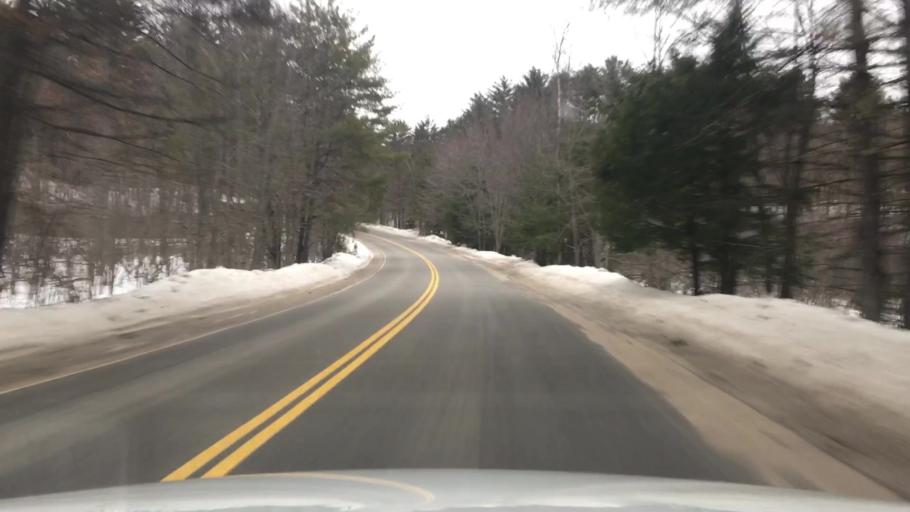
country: US
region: Maine
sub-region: Oxford County
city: Hiram
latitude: 43.8904
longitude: -70.7901
